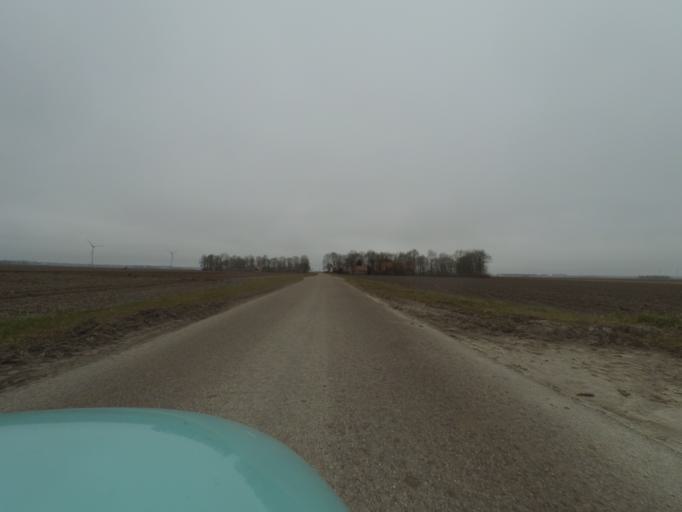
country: NL
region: Flevoland
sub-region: Gemeente Dronten
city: Dronten
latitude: 52.4756
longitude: 5.7535
